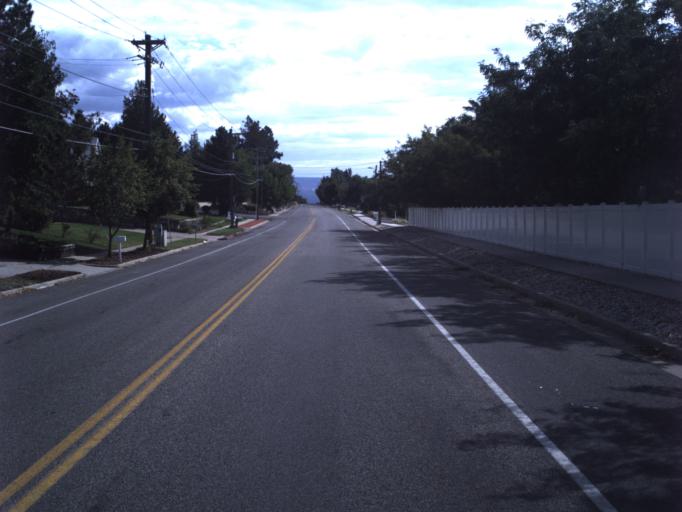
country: US
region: Utah
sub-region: Davis County
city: Farmington
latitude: 40.9681
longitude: -111.8834
